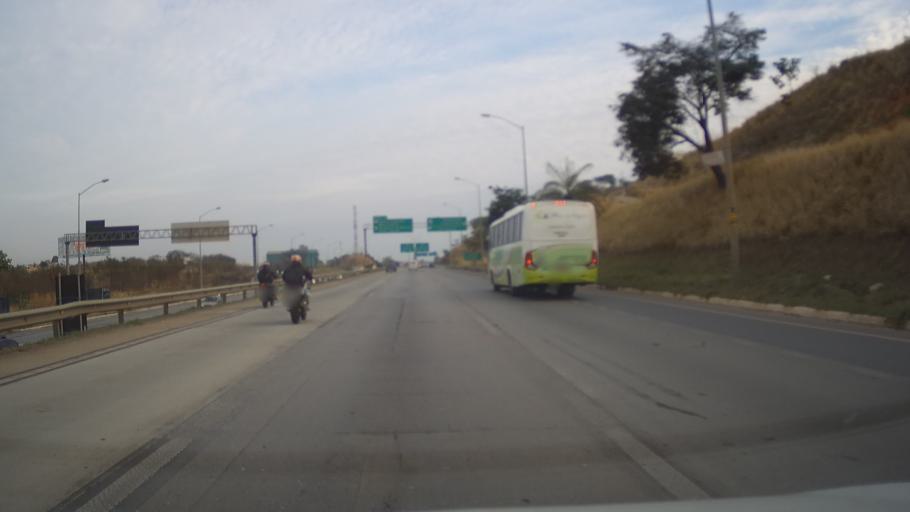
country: BR
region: Minas Gerais
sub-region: Vespasiano
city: Vespasiano
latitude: -19.7661
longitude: -43.9482
